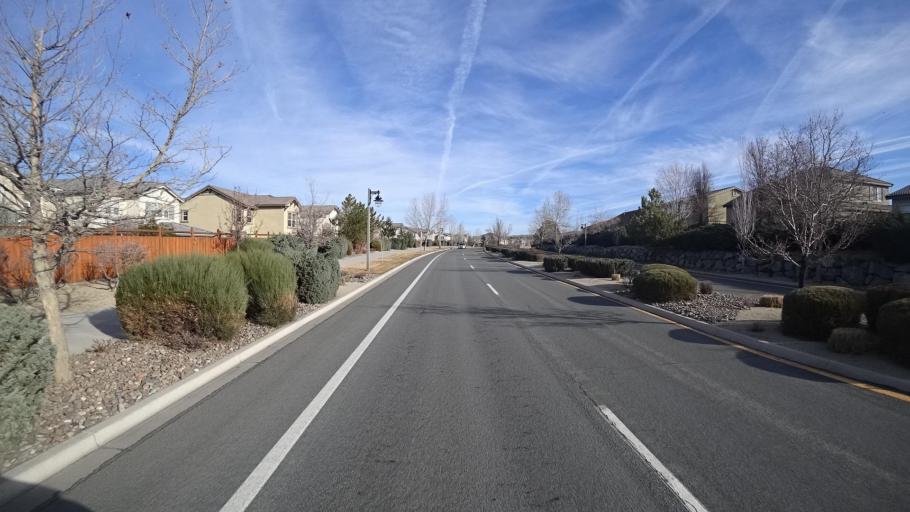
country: US
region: Nevada
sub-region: Washoe County
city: Spanish Springs
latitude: 39.6153
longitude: -119.6706
